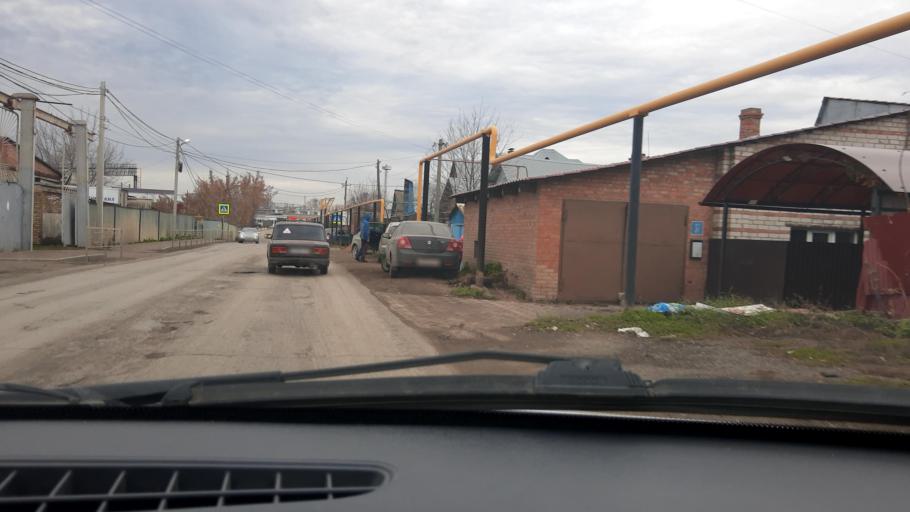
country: RU
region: Bashkortostan
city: Mikhaylovka
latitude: 54.6983
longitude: 55.8493
